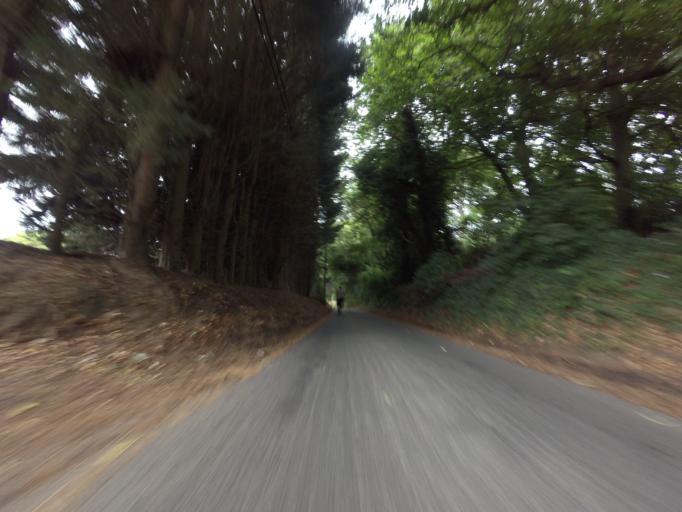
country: GB
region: England
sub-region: Kent
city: West Malling
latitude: 51.3013
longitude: 0.4093
